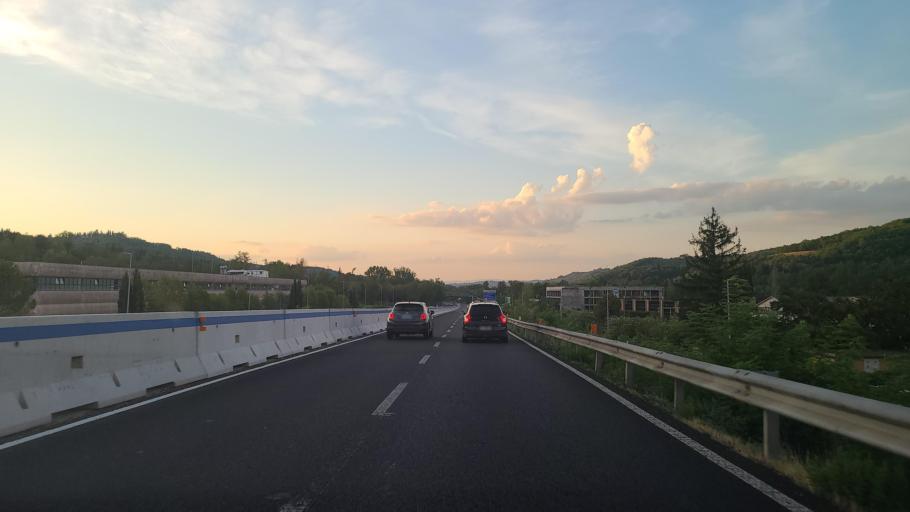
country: IT
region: Tuscany
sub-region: Province of Florence
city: Sambuca
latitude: 43.5885
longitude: 11.2011
